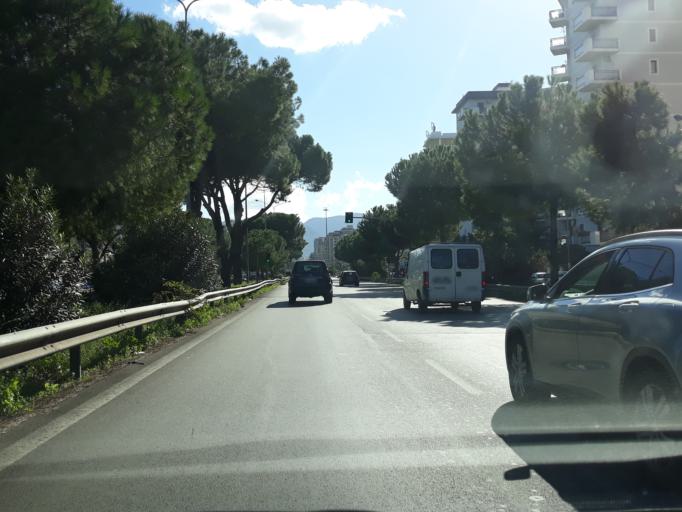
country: IT
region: Sicily
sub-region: Palermo
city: Palermo
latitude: 38.1333
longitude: 13.3303
